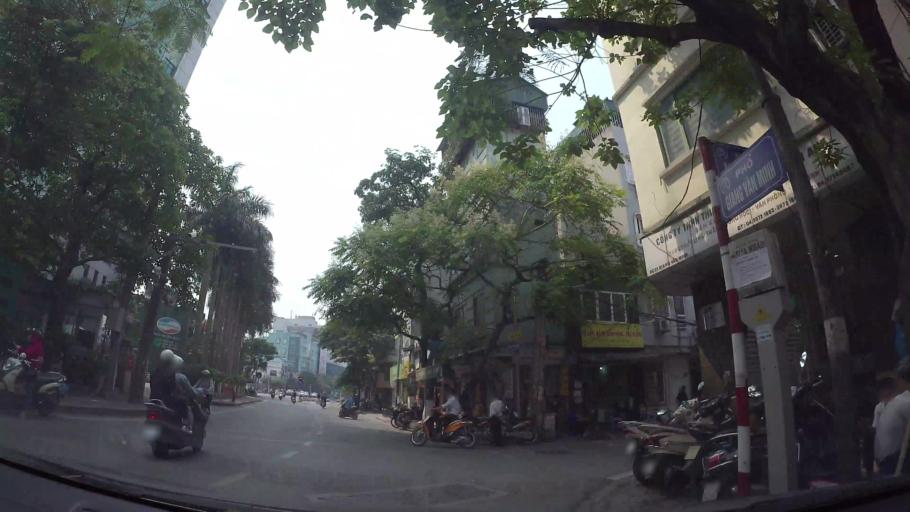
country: VN
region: Ha Noi
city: Dong Da
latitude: 21.0303
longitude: 105.8269
